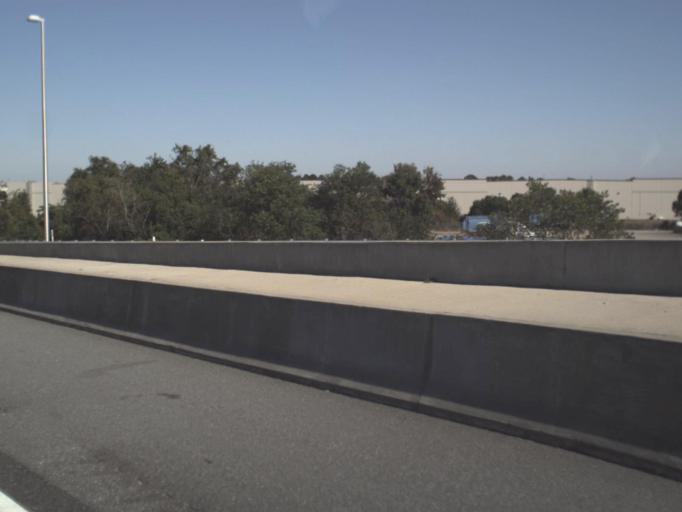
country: US
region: Florida
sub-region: Orange County
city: Sky Lake
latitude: 28.4385
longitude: -81.3986
